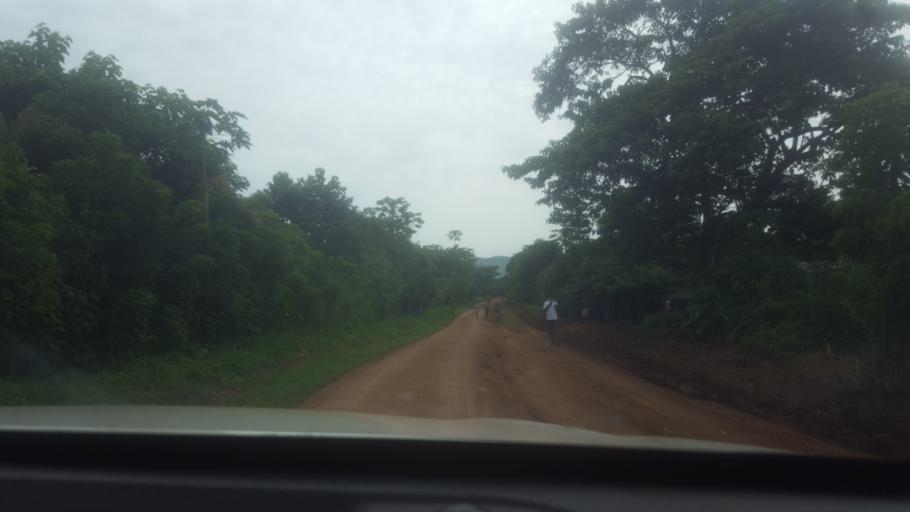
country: ET
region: Southern Nations, Nationalities, and People's Region
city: Tippi
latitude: 7.4476
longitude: 35.0472
